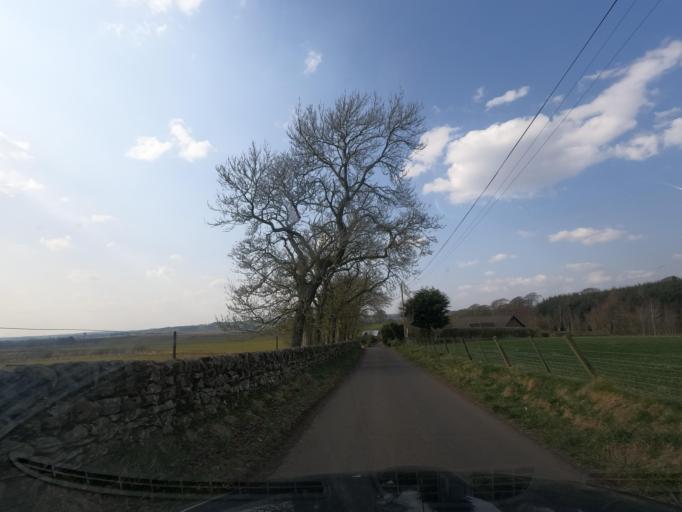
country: GB
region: Scotland
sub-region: South Lanarkshire
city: Carnwath
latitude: 55.7370
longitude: -3.6101
